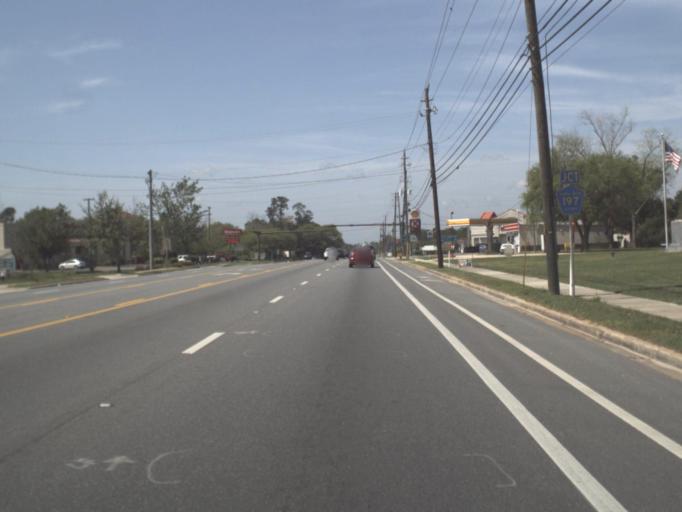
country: US
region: Florida
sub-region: Santa Rosa County
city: Pace
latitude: 30.6002
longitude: -87.1594
